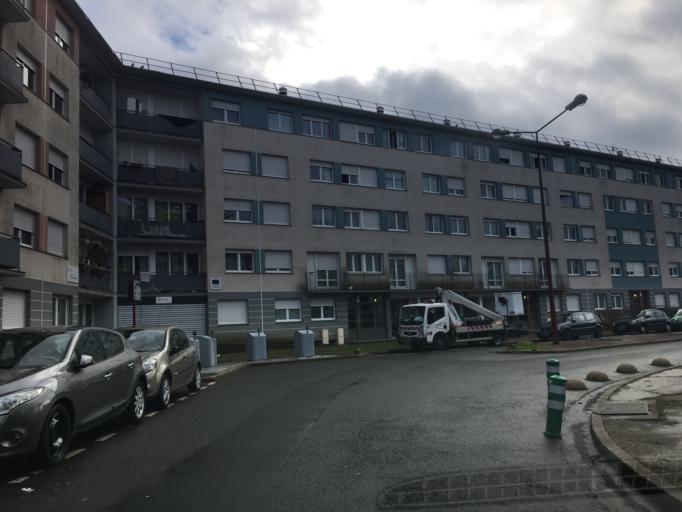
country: FR
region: Ile-de-France
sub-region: Departement du Val-d'Oise
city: Arnouville
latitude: 49.0031
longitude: 2.4205
